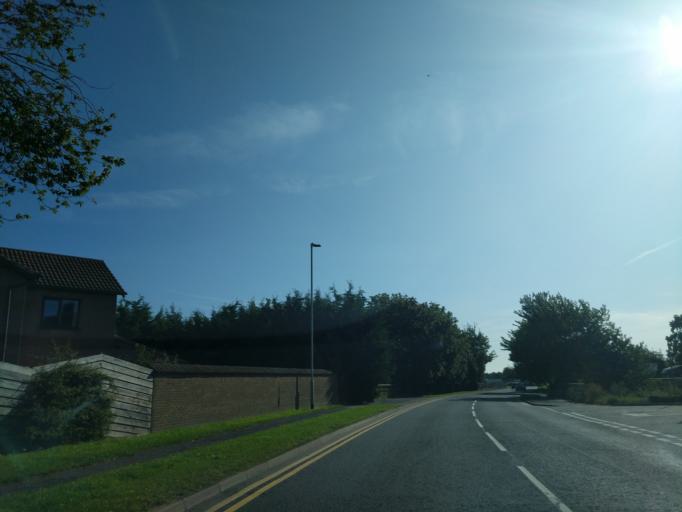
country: GB
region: England
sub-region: Lincolnshire
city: Bourne
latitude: 52.7603
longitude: -0.3665
